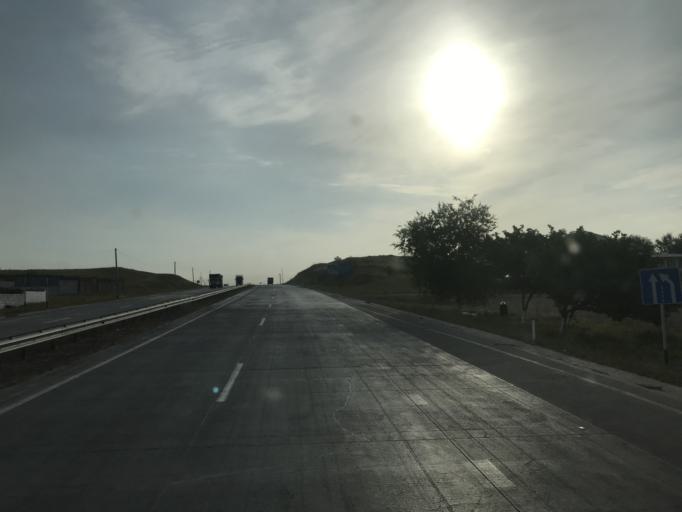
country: UZ
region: Toshkent
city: Salor
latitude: 41.5054
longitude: 69.3723
